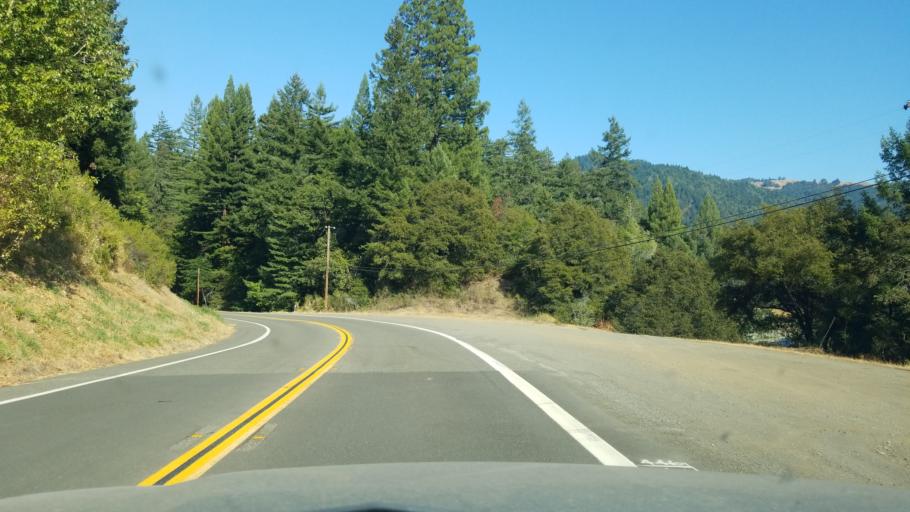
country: US
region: California
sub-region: Humboldt County
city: Redway
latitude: 40.2220
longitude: -123.8064
